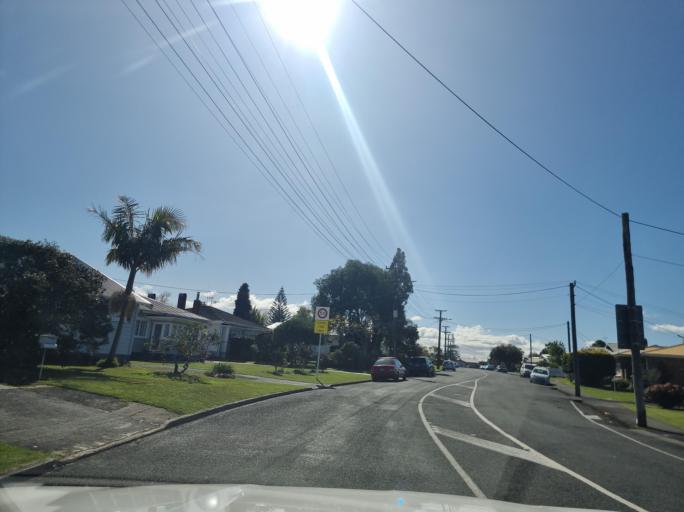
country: NZ
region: Northland
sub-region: Whangarei
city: Whangarei
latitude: -35.7143
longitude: 174.3210
